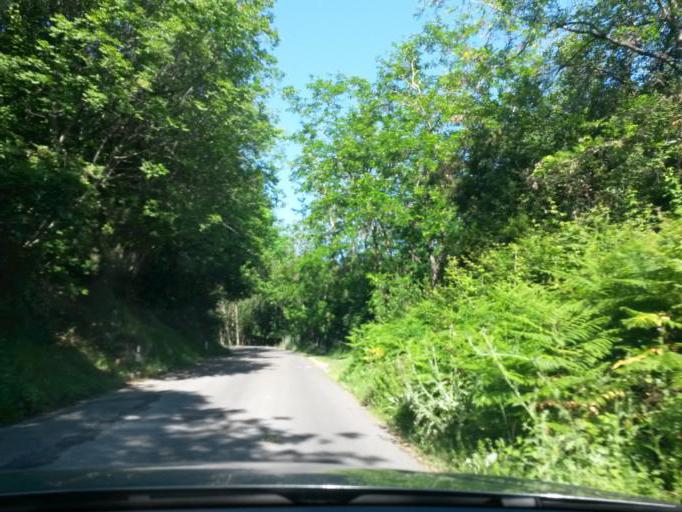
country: IT
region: Tuscany
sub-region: Provincia di Livorno
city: Marciana Marina
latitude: 42.7915
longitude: 10.1849
